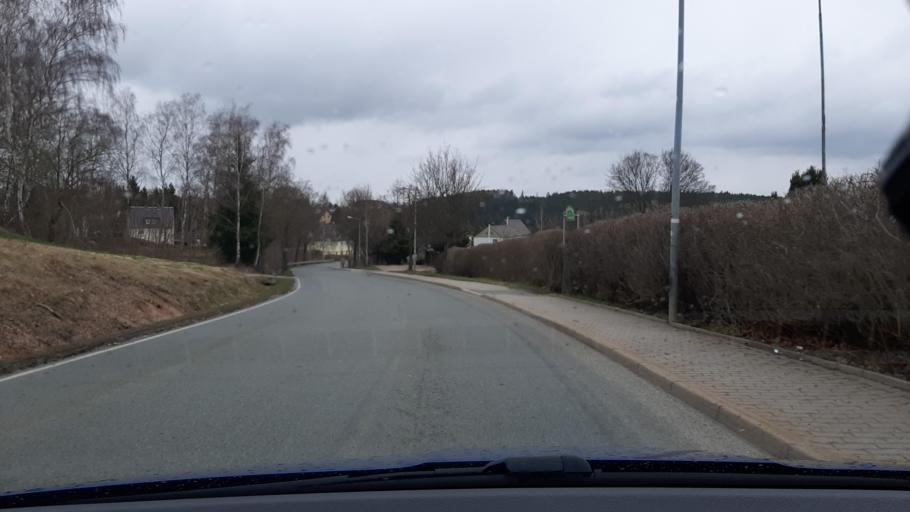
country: DE
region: Saxony
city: Schoenheide
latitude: 50.5088
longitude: 12.5252
